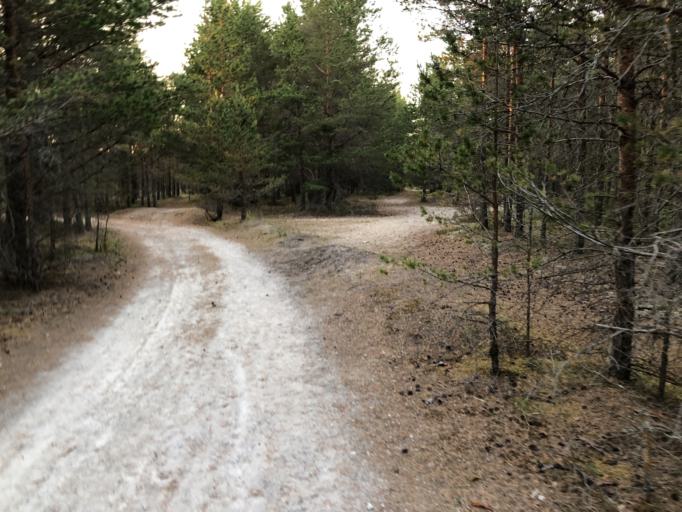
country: EE
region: Harju
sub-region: Paldiski linn
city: Paldiski
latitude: 59.3914
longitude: 24.2332
